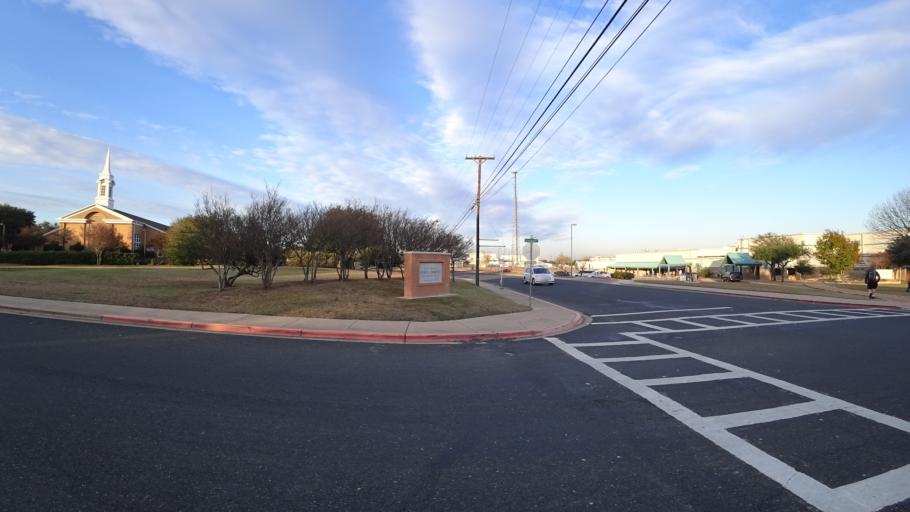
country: US
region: Texas
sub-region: Williamson County
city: Brushy Creek
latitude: 30.4920
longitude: -97.7355
